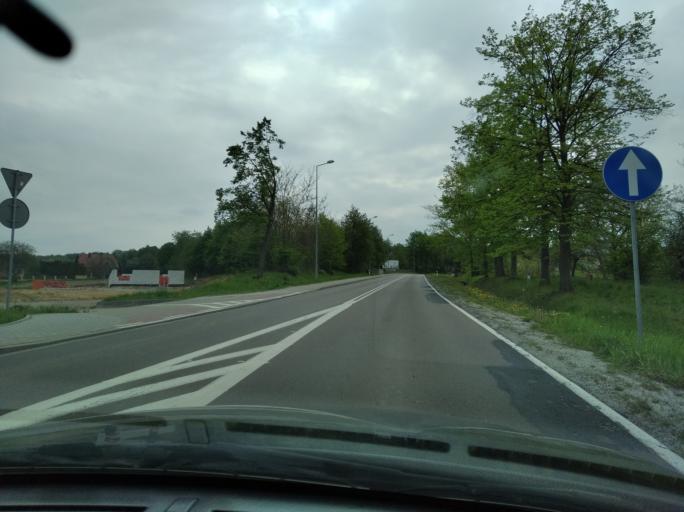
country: PL
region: Lesser Poland Voivodeship
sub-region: Powiat tarnowski
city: Tarnowiec
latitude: 49.9705
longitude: 20.9929
